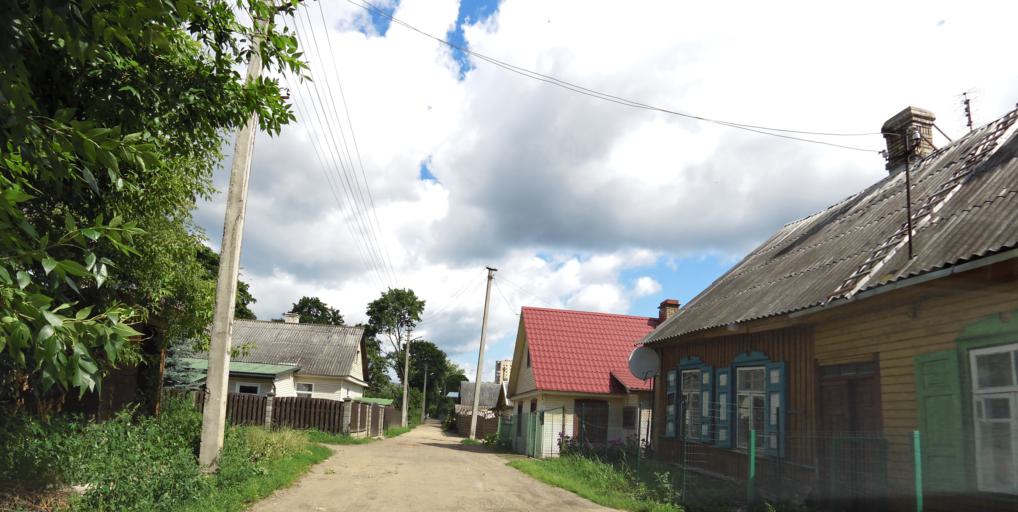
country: LT
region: Vilnius County
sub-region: Vilnius
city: Vilnius
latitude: 54.7010
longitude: 25.2804
